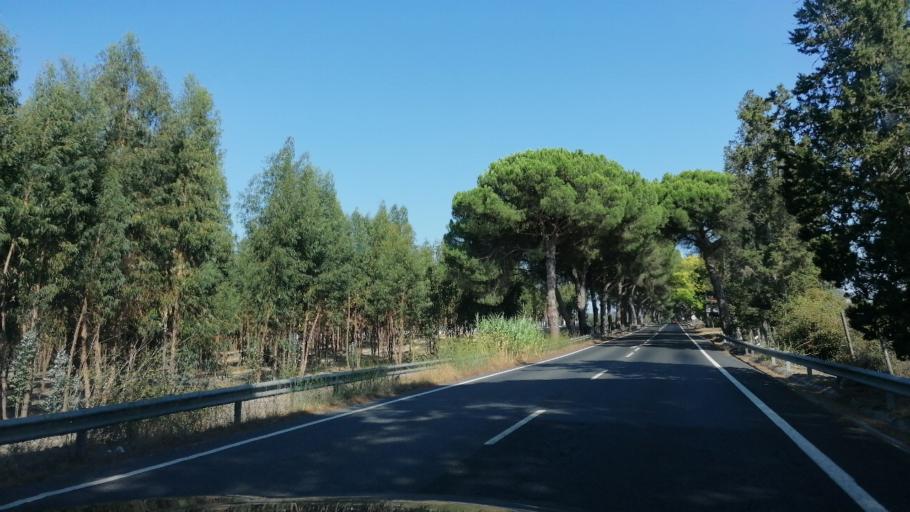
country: PT
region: Evora
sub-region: Vendas Novas
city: Vendas Novas
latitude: 38.7208
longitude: -8.6313
